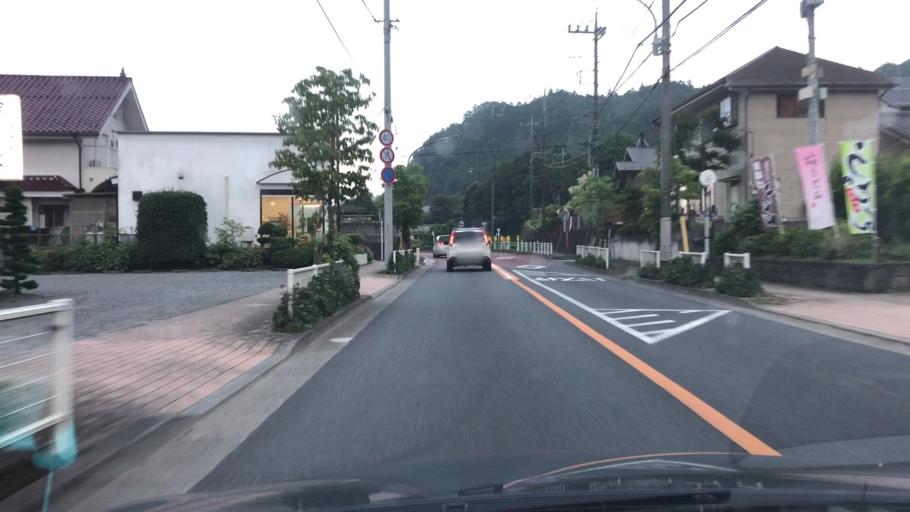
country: JP
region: Tokyo
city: Ome
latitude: 35.7951
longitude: 139.2142
